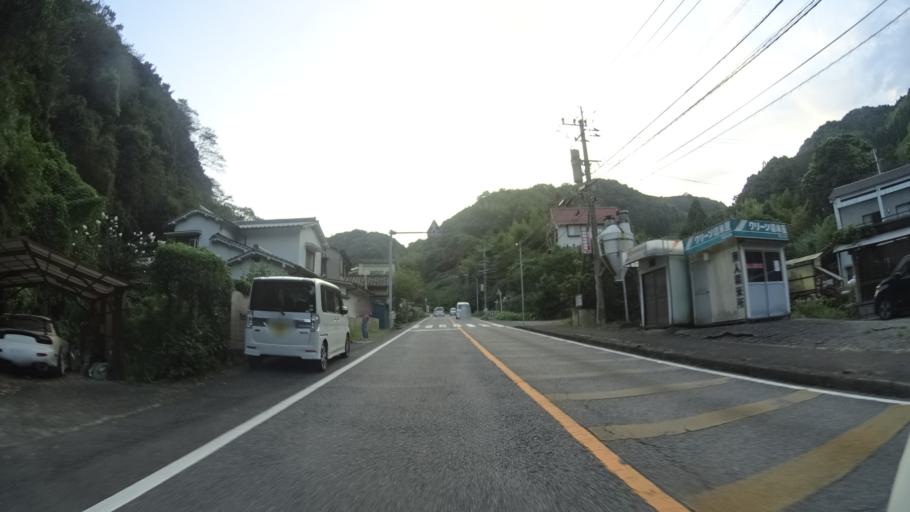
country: JP
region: Oita
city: Beppu
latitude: 33.3286
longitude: 131.4777
